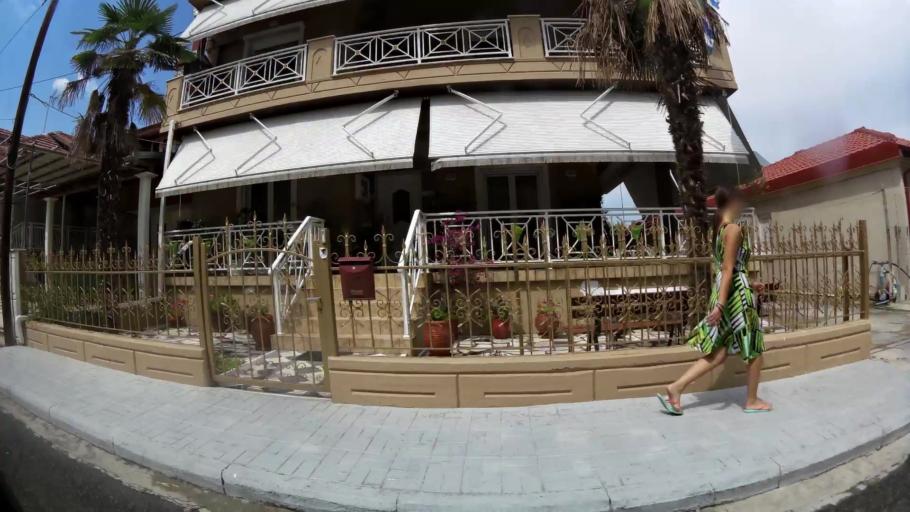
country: GR
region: Central Macedonia
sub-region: Nomos Pierias
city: Korinos
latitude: 40.3126
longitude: 22.5767
